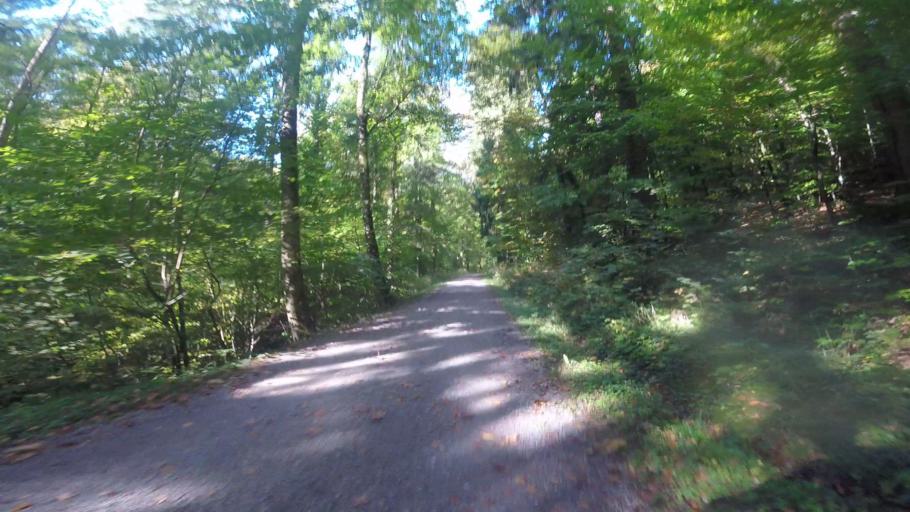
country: DE
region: Baden-Wuerttemberg
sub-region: Regierungsbezirk Stuttgart
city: Oberstenfeld
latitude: 48.9903
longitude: 9.3284
